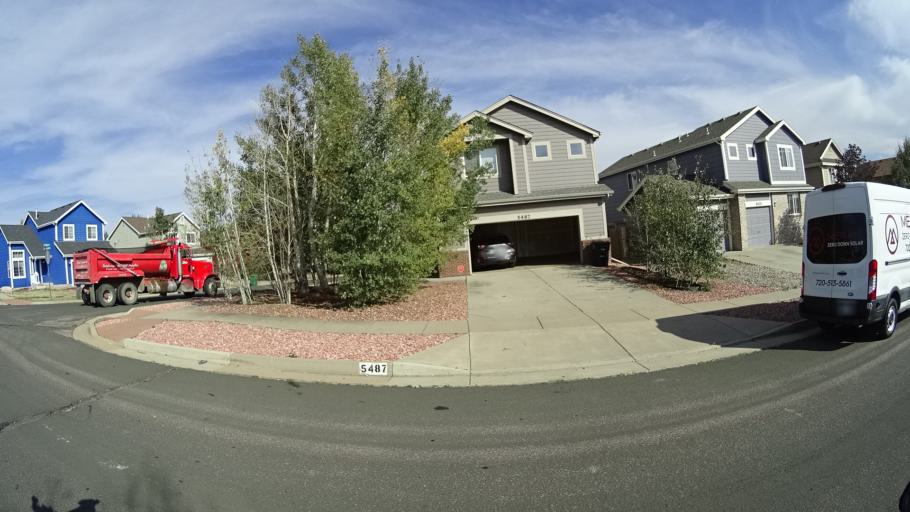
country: US
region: Colorado
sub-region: El Paso County
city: Cimarron Hills
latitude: 38.9114
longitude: -104.6911
